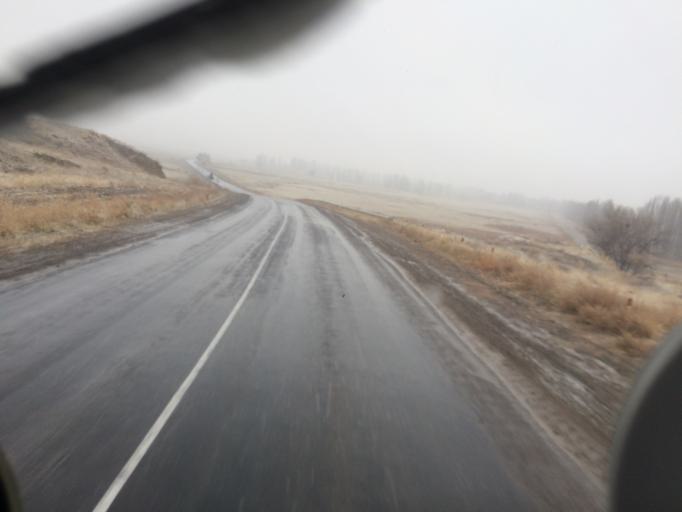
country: KG
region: Chuy
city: Ivanovka
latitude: 42.9640
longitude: 75.0030
